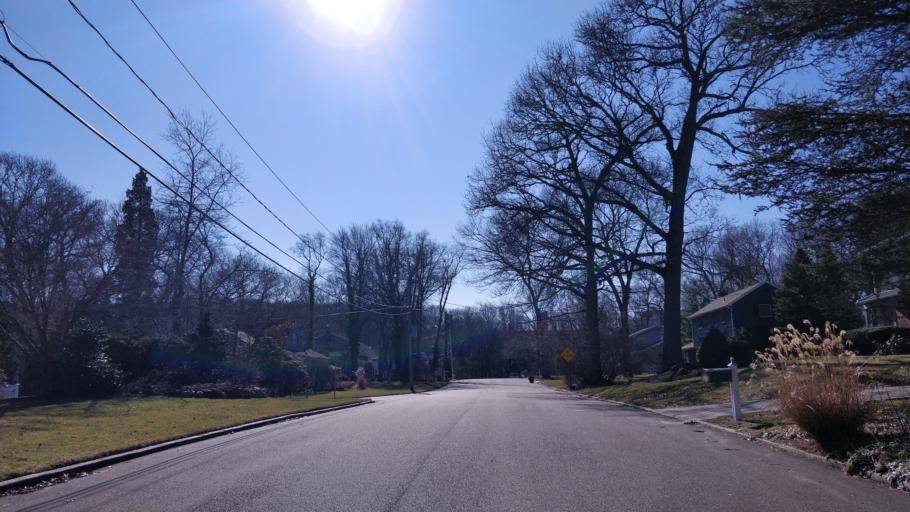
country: US
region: New York
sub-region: Suffolk County
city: Setauket-East Setauket
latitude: 40.9123
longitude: -73.1115
